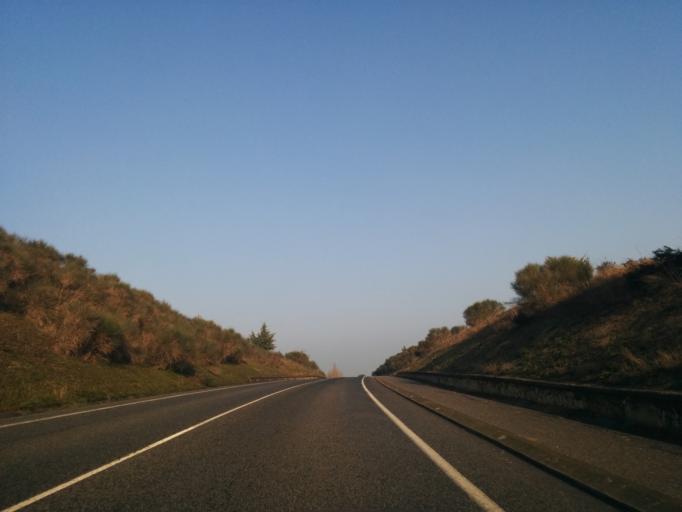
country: ES
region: Navarre
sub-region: Provincia de Navarra
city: Elorz
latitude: 42.7649
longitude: -1.5814
